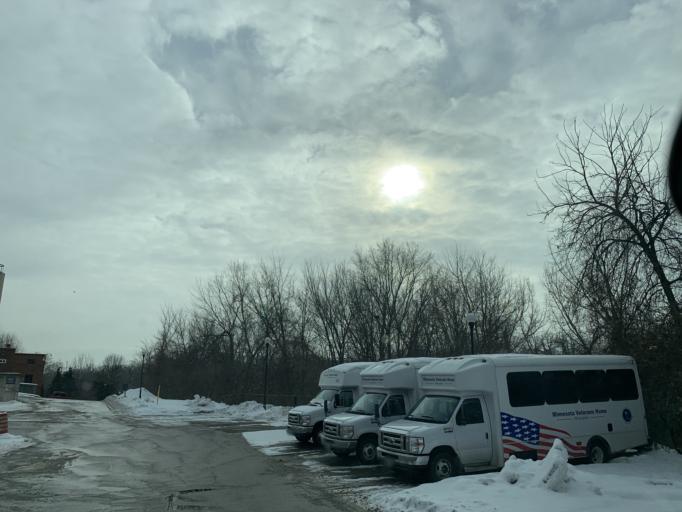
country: US
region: Minnesota
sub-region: Dakota County
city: Mendota Heights
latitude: 44.9123
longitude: -93.2053
